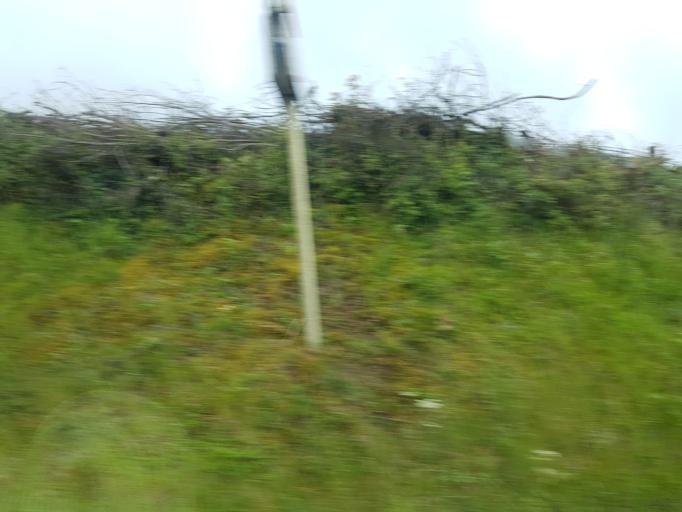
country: FR
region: Bourgogne
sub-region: Departement de la Nievre
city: Chateau-Chinon(Ville)
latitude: 47.0451
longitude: 4.0295
